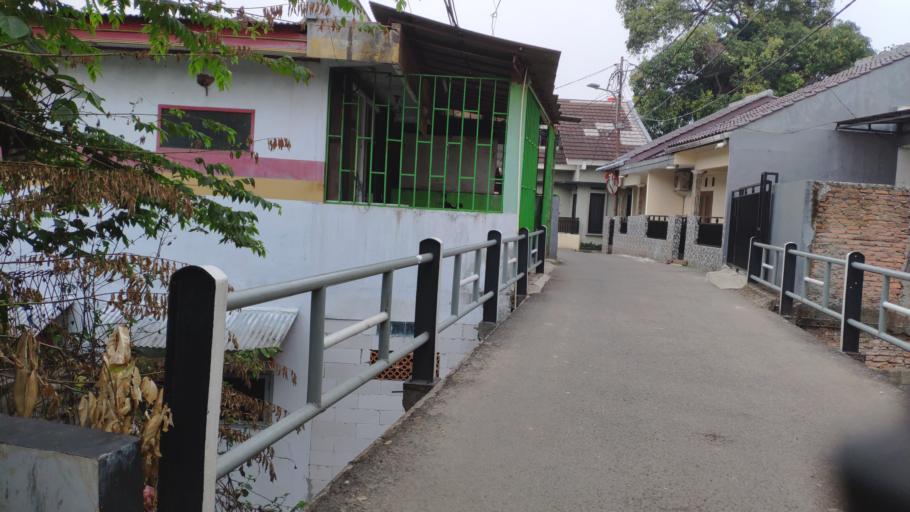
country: ID
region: West Java
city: Depok
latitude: -6.3163
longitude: 106.8360
